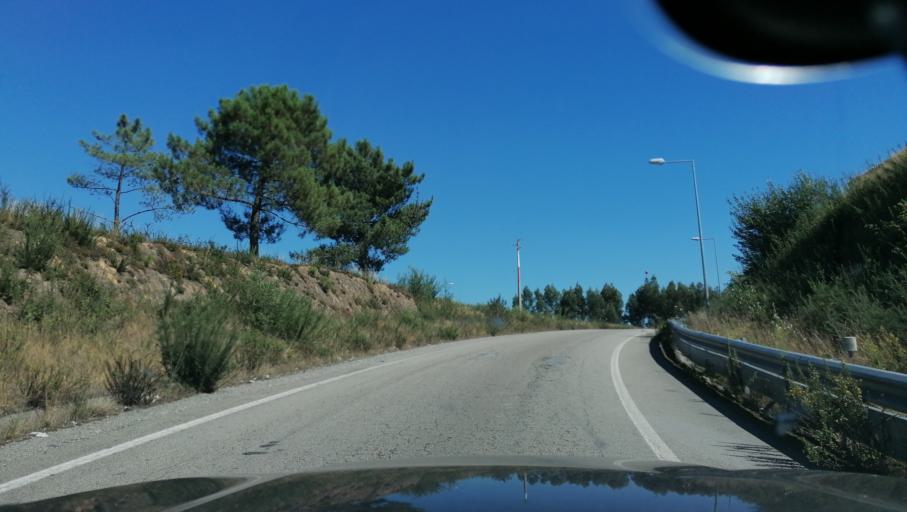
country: PT
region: Aveiro
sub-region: Santa Maria da Feira
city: Arrifana
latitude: 40.9249
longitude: -8.5036
